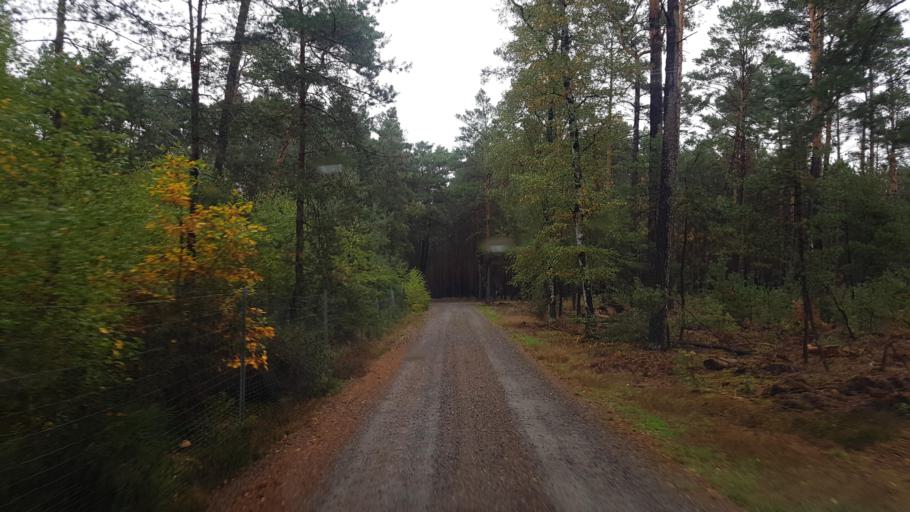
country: DE
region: Brandenburg
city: Schlieben
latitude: 51.7787
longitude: 13.3481
